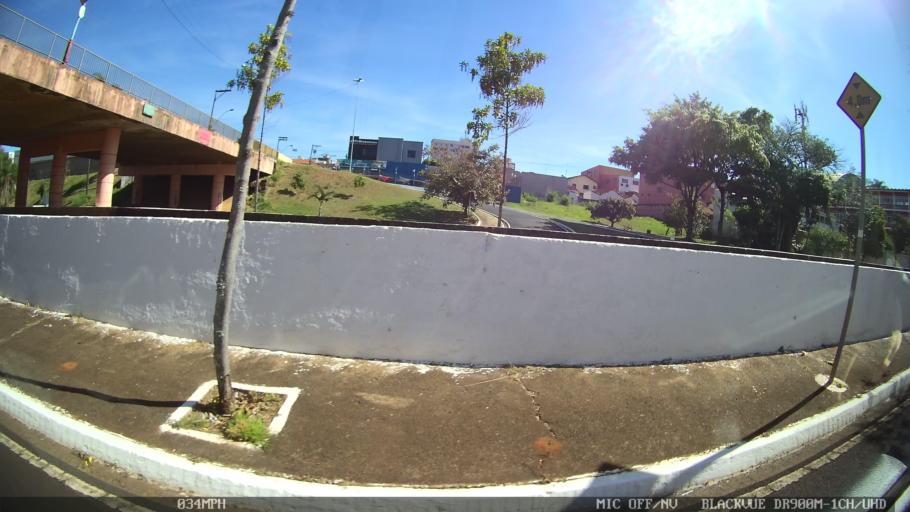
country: BR
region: Sao Paulo
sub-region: Franca
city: Franca
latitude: -20.5343
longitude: -47.4059
